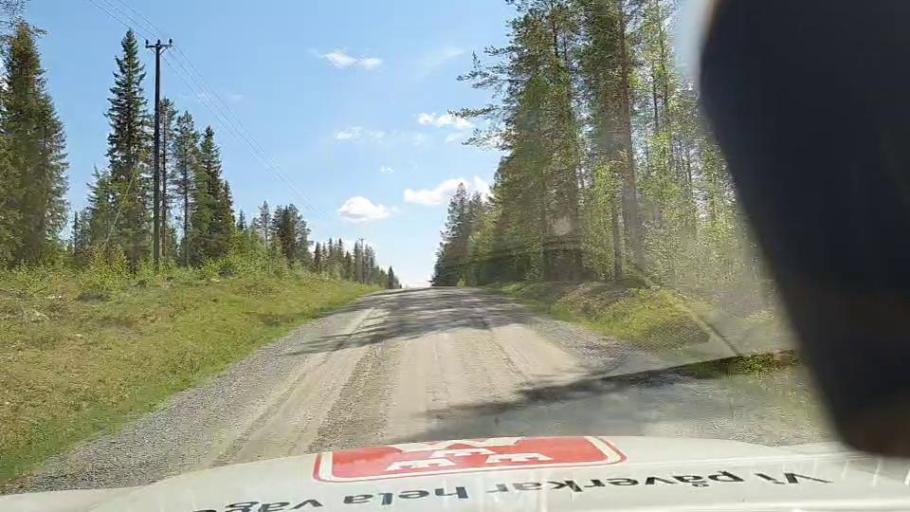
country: SE
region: Jaemtland
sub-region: Stroemsunds Kommun
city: Stroemsund
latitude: 64.4821
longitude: 15.5922
